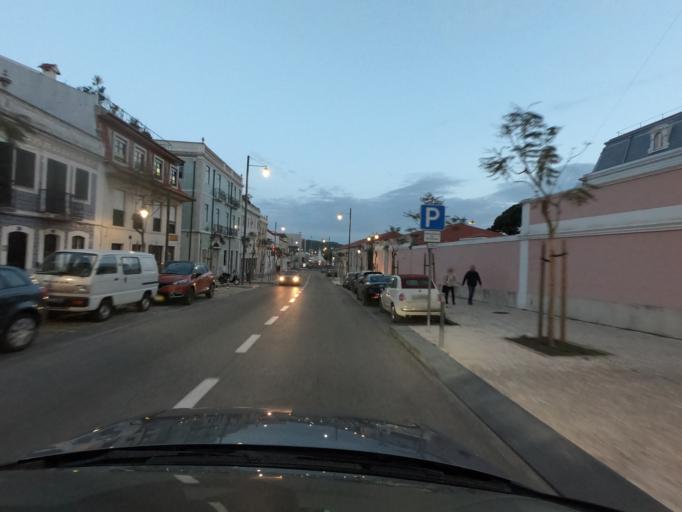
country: PT
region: Lisbon
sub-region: Oeiras
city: Alges
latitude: 38.6987
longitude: -9.1996
